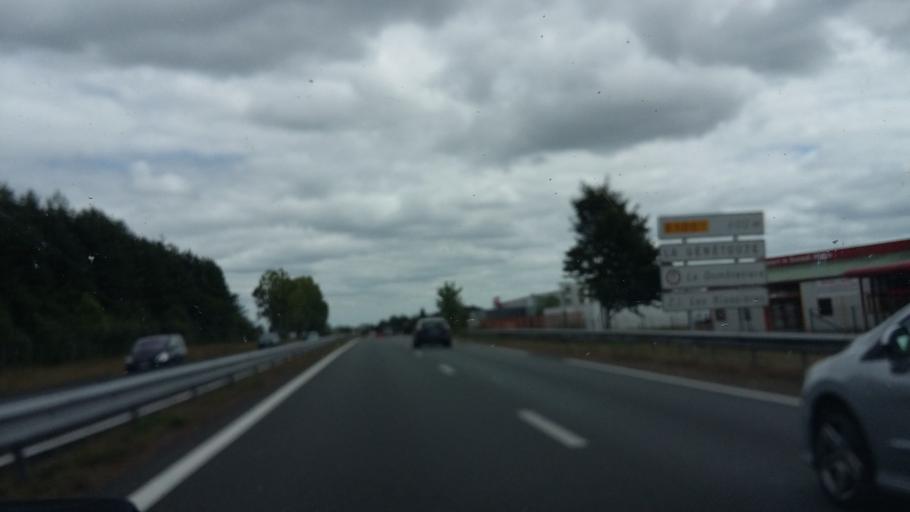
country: FR
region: Pays de la Loire
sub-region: Departement de la Vendee
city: Aizenay
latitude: 46.7263
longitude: -1.5696
